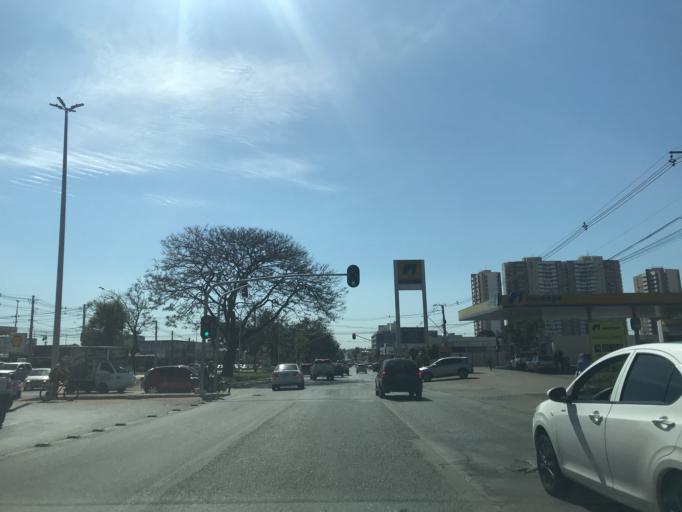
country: BR
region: Federal District
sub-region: Brasilia
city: Brasilia
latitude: -15.8085
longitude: -48.0845
